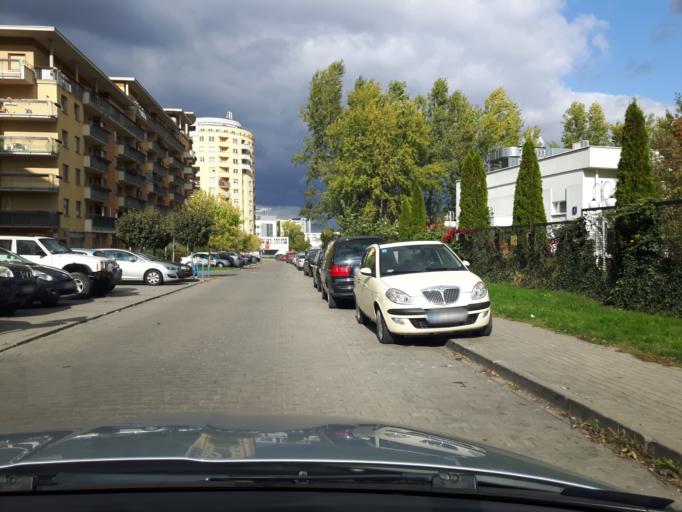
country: PL
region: Masovian Voivodeship
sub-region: Warszawa
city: Ursynow
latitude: 52.1434
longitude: 21.0363
